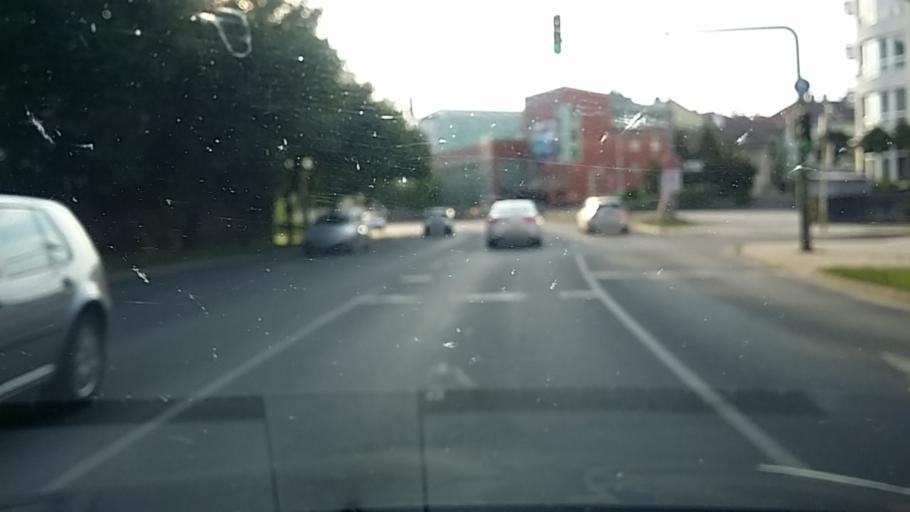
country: HU
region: Borsod-Abauj-Zemplen
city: Miskolc
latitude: 48.1014
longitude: 20.7833
